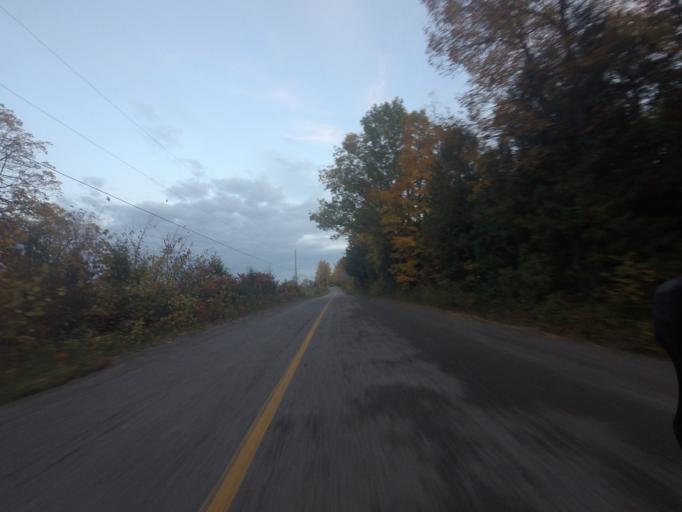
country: CA
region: Ontario
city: Renfrew
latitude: 45.3498
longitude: -76.9465
